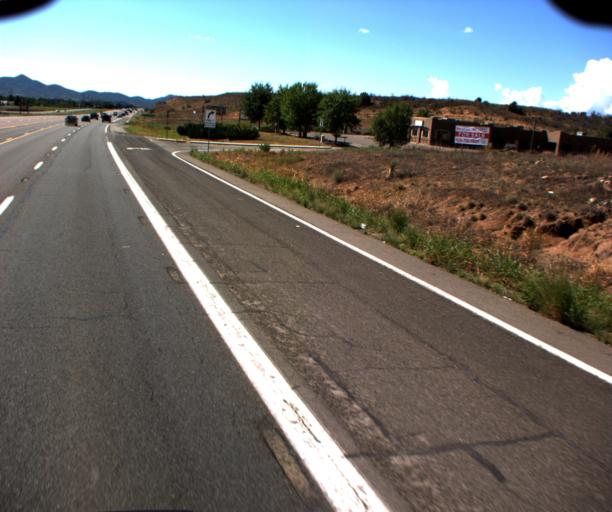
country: US
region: Arizona
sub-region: Yavapai County
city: Dewey-Humboldt
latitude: 34.5556
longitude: -112.2542
